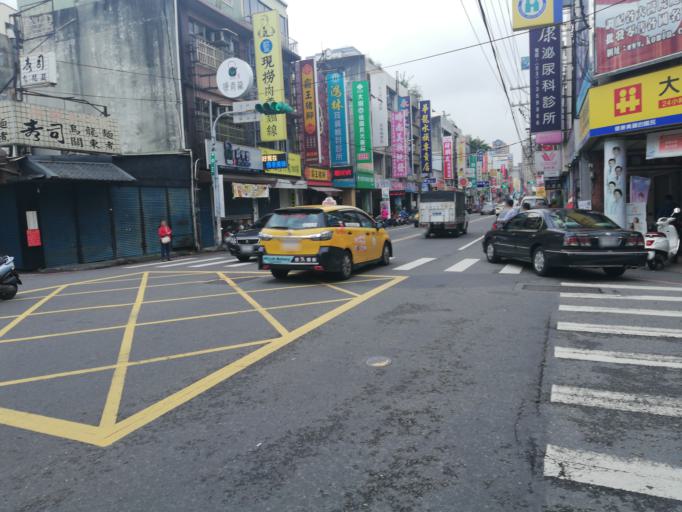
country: TW
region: Taiwan
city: Taoyuan City
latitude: 25.0038
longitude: 121.3053
